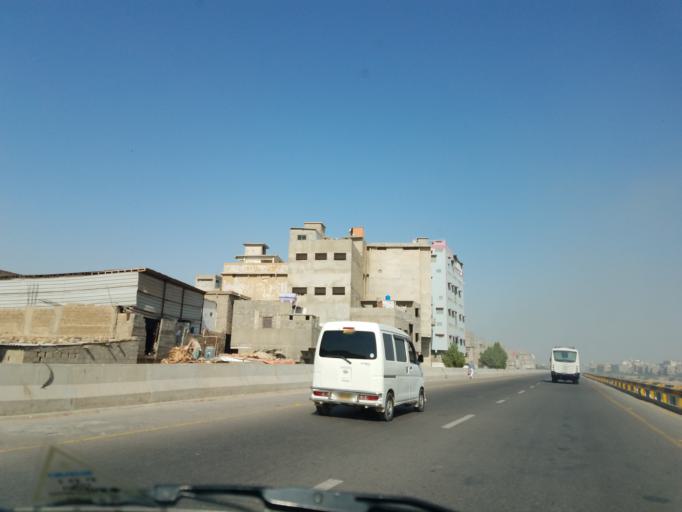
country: PK
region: Sindh
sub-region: Karachi District
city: Karachi
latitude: 24.9118
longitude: 67.0694
